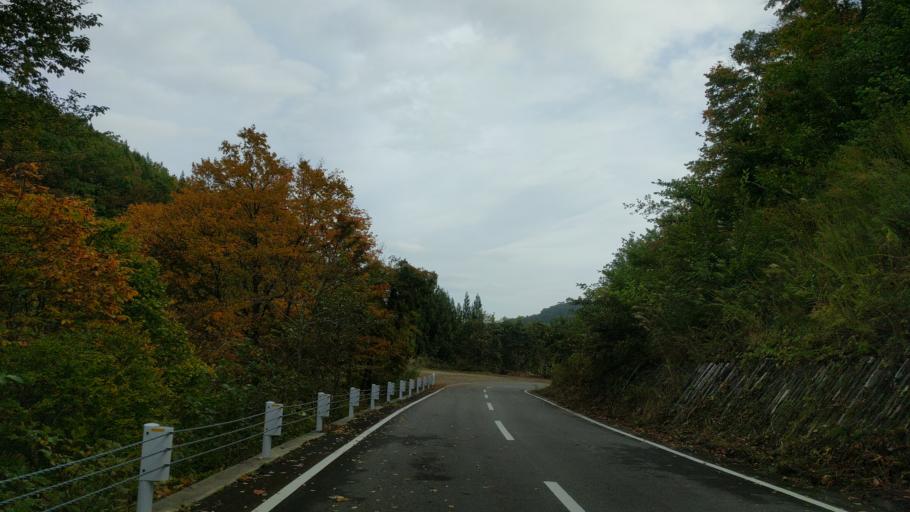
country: JP
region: Fukushima
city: Kitakata
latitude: 37.3842
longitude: 139.6980
